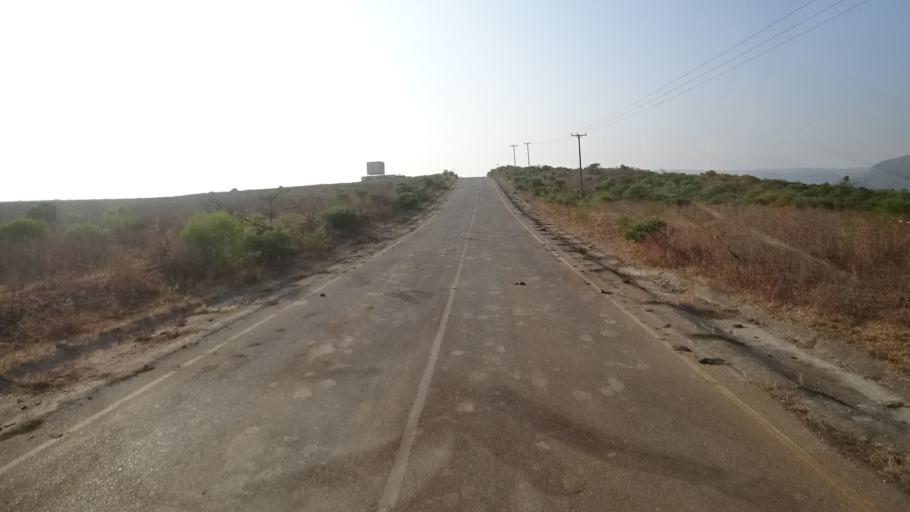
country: YE
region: Al Mahrah
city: Hawf
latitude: 16.7455
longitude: 53.3482
